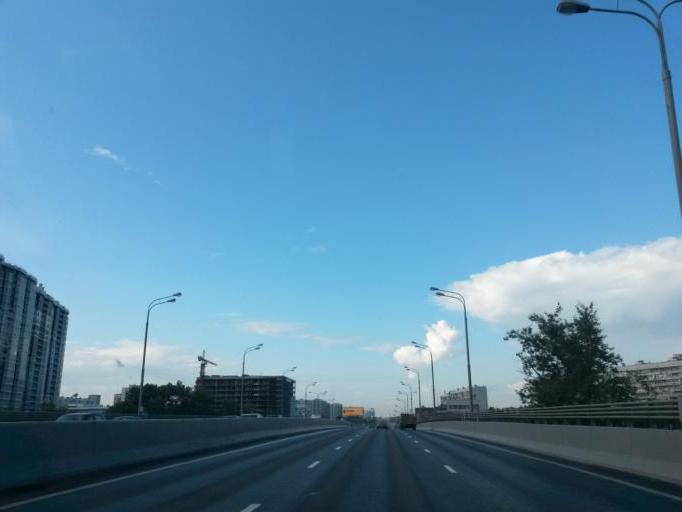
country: RU
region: Moscow
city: Chertanovo Yuzhnoye
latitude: 55.5943
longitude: 37.6016
